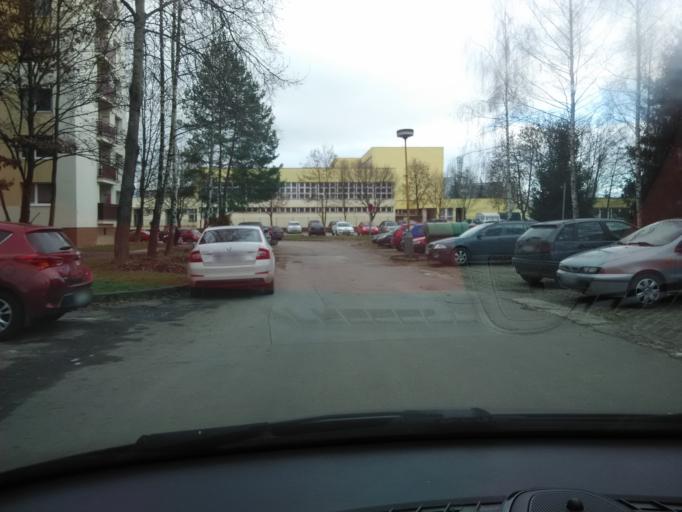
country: SK
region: Zilinsky
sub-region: Okres Zilina
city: Zilina
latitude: 49.2048
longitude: 18.7676
